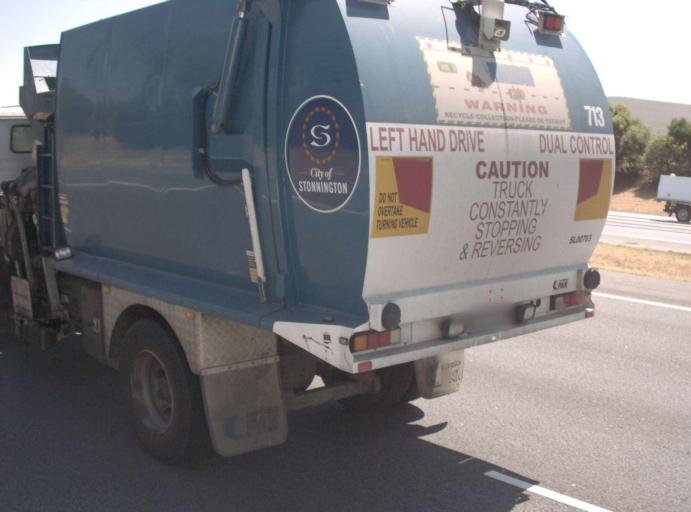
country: AU
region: Victoria
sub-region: Monash
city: Mulgrave
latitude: -37.9249
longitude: 145.1790
